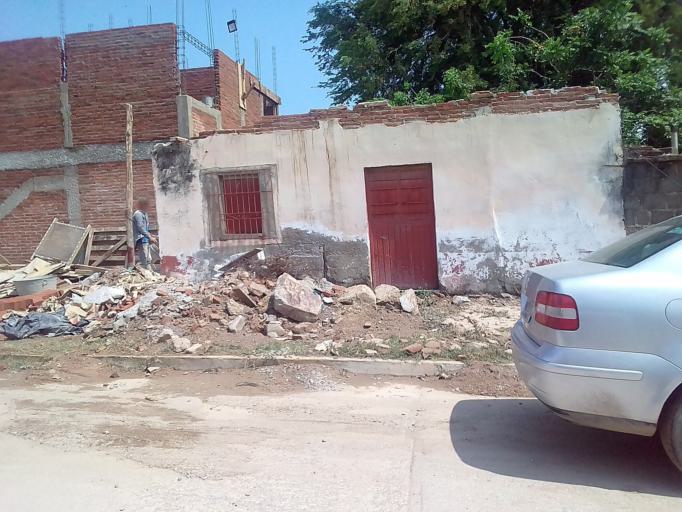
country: MX
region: Oaxaca
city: Union Hidalgo
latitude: 16.4700
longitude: -94.8322
